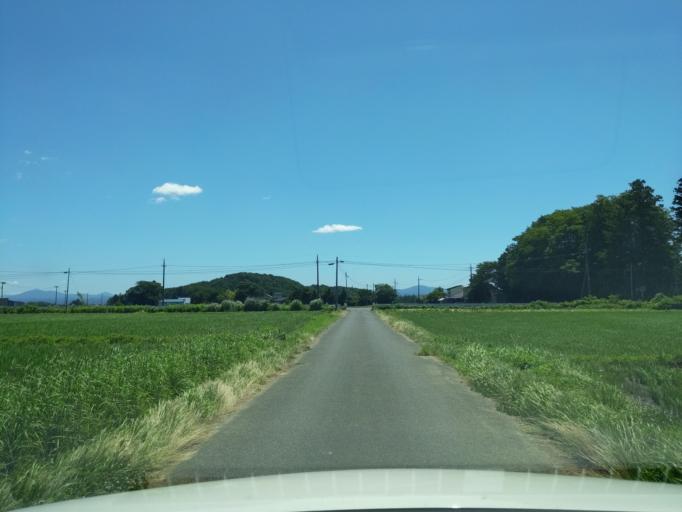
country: JP
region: Fukushima
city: Koriyama
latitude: 37.3986
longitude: 140.2885
